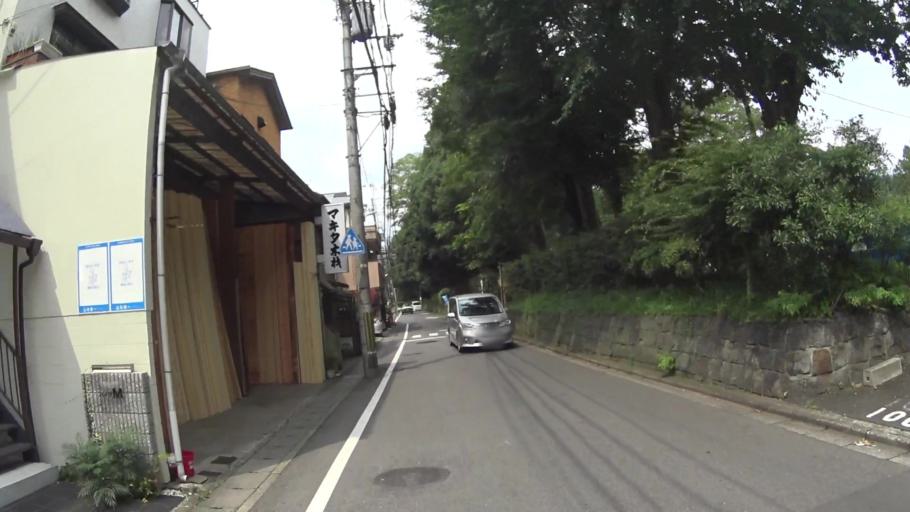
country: JP
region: Kyoto
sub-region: Kyoto-shi
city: Kamigyo-ku
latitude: 35.0603
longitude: 135.7512
